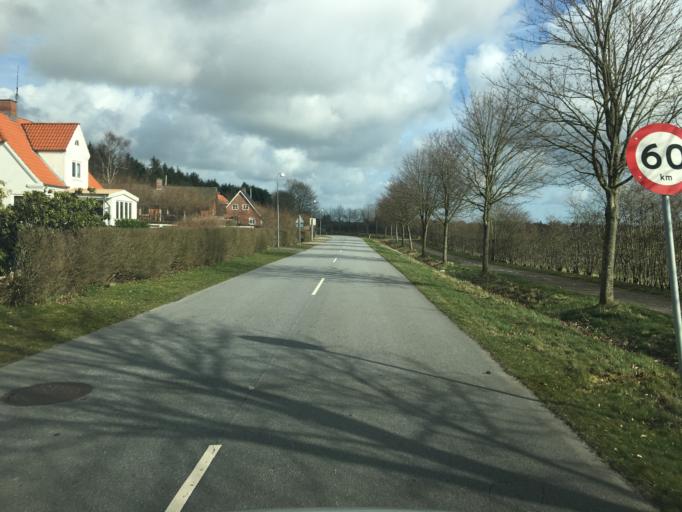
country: DK
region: South Denmark
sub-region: Aabenraa Kommune
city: Krusa
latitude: 54.8975
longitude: 9.4466
